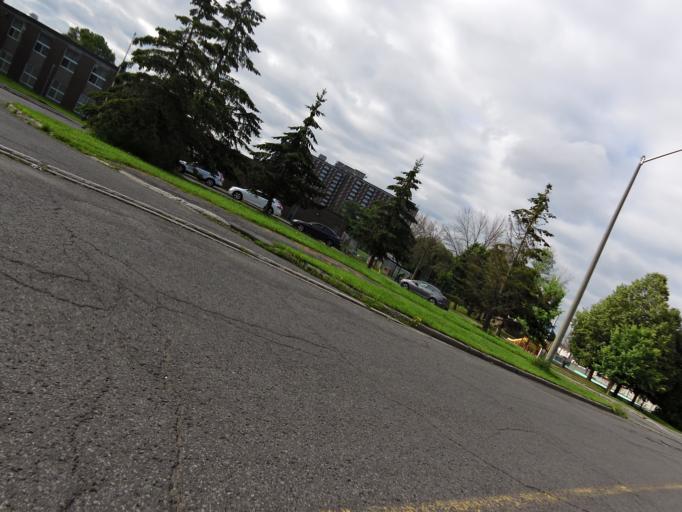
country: CA
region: Ontario
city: Bells Corners
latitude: 45.3523
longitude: -75.7954
